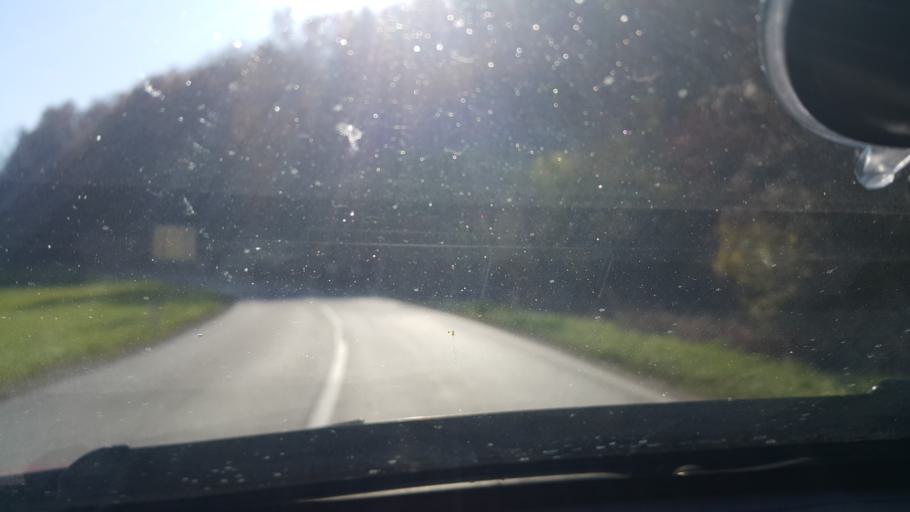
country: SI
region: Podcetrtek
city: Podcetrtek
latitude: 46.1157
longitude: 15.5986
